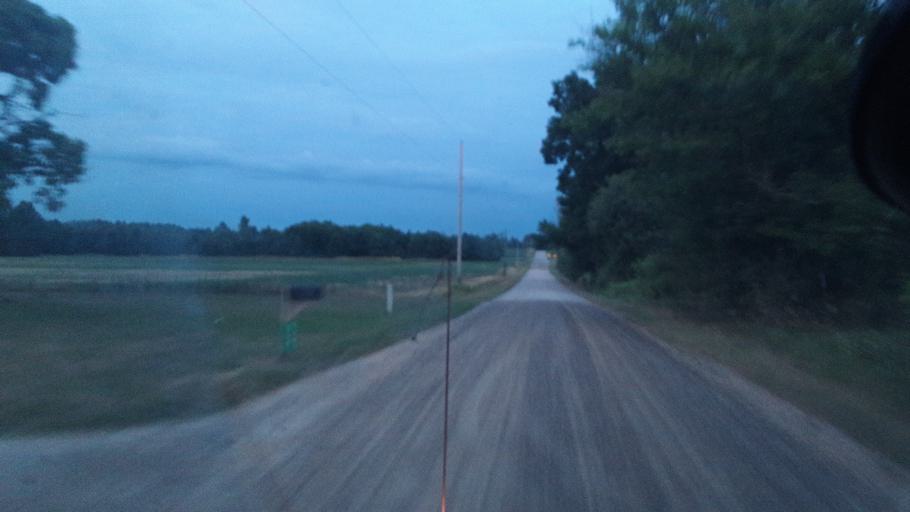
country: US
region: Ohio
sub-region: Defiance County
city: Hicksville
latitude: 41.3438
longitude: -84.8305
